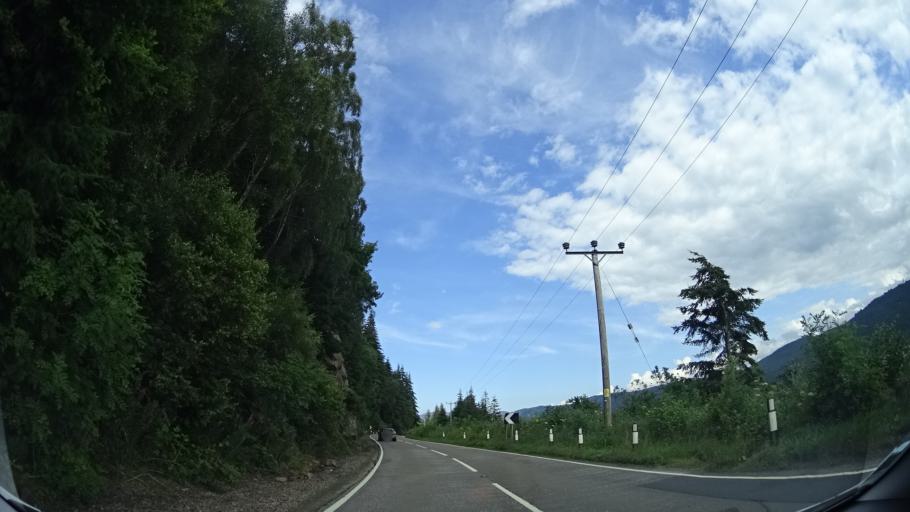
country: GB
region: Scotland
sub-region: Highland
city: Beauly
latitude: 57.2464
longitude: -4.5403
